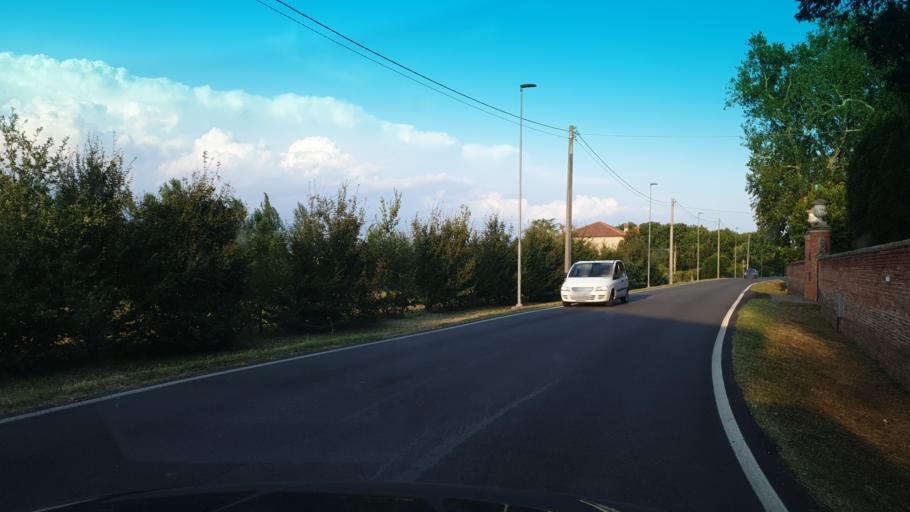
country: IT
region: Veneto
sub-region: Provincia di Rovigo
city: Castelguglielmo
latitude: 45.0313
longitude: 11.5531
